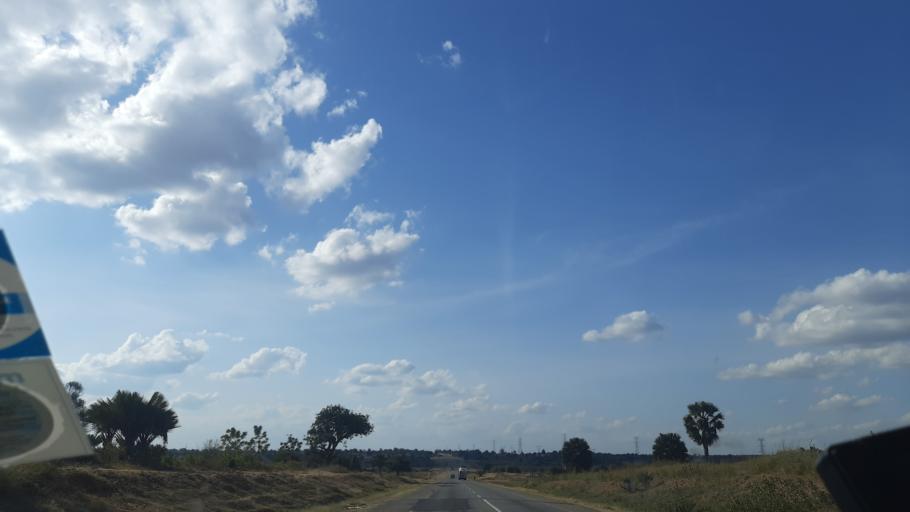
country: TZ
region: Singida
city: Ikungi
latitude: -5.1033
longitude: 34.7654
